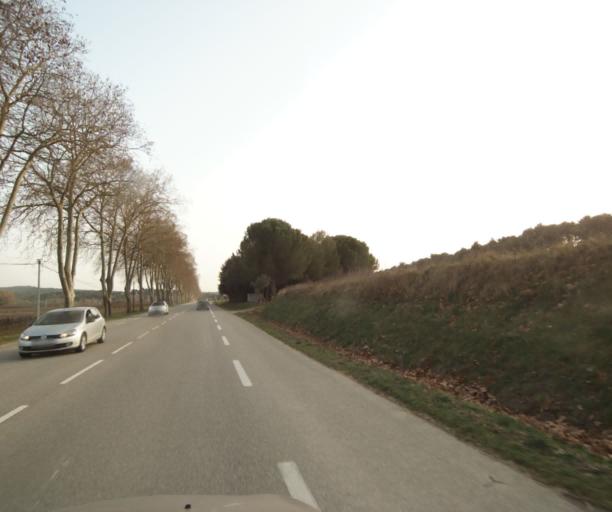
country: FR
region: Provence-Alpes-Cote d'Azur
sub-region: Departement des Bouches-du-Rhone
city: Rognes
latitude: 43.6501
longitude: 5.3578
